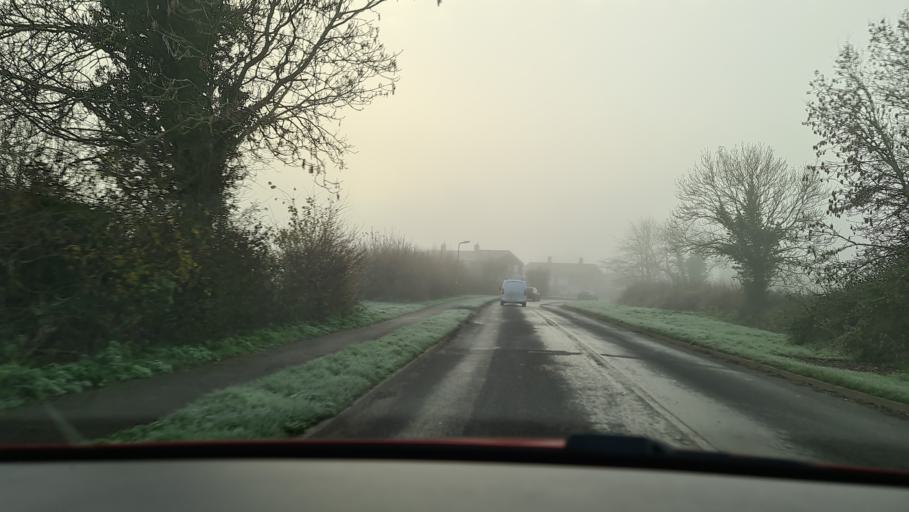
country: GB
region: England
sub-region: Buckinghamshire
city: Waddesdon
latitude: 51.8447
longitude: -0.9556
